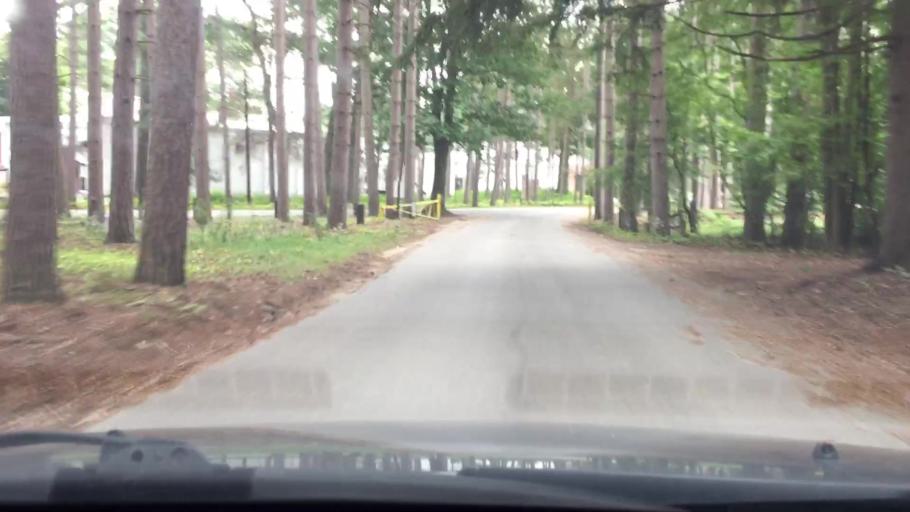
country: US
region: New Hampshire
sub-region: Cheshire County
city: Keene
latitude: 42.9402
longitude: -72.3047
